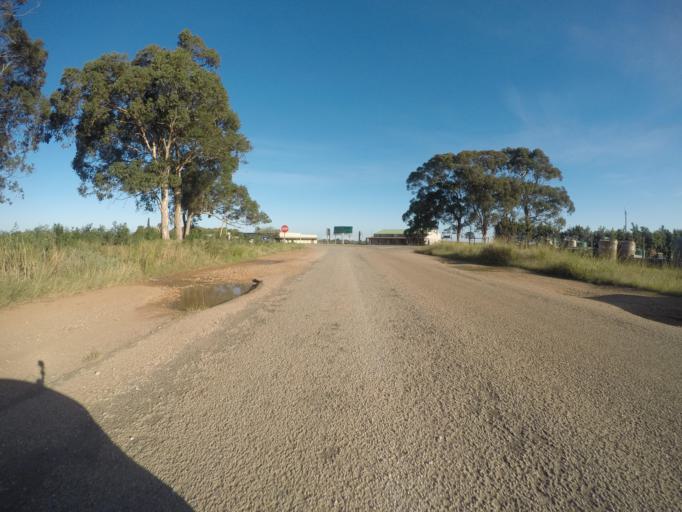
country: ZA
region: Eastern Cape
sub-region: Cacadu District Municipality
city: Kareedouw
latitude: -34.0046
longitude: 24.2342
